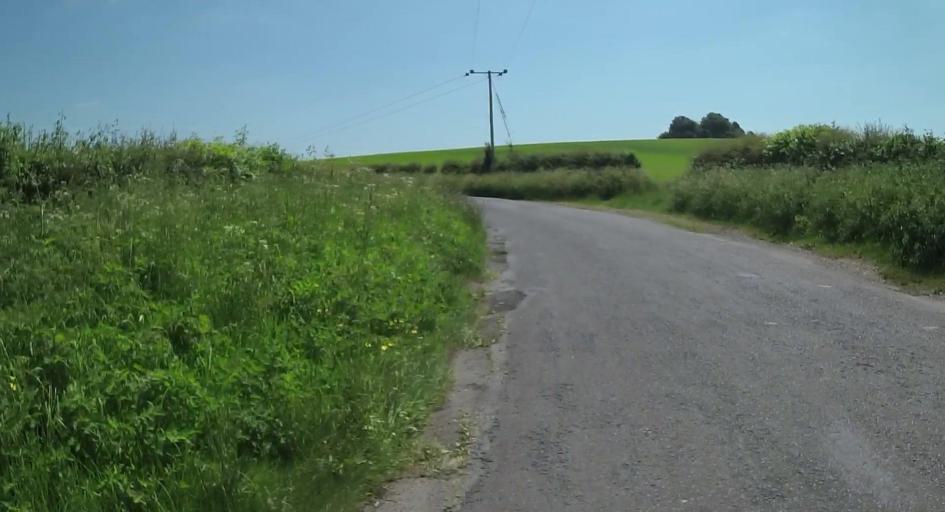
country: GB
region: England
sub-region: Hampshire
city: Kings Worthy
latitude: 51.0723
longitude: -1.2704
